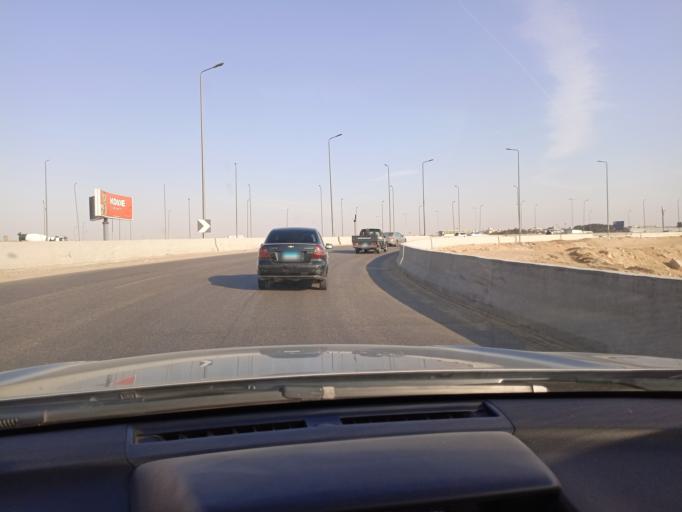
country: EG
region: Muhafazat al Qalyubiyah
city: Al Khankah
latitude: 30.0820
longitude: 31.4348
